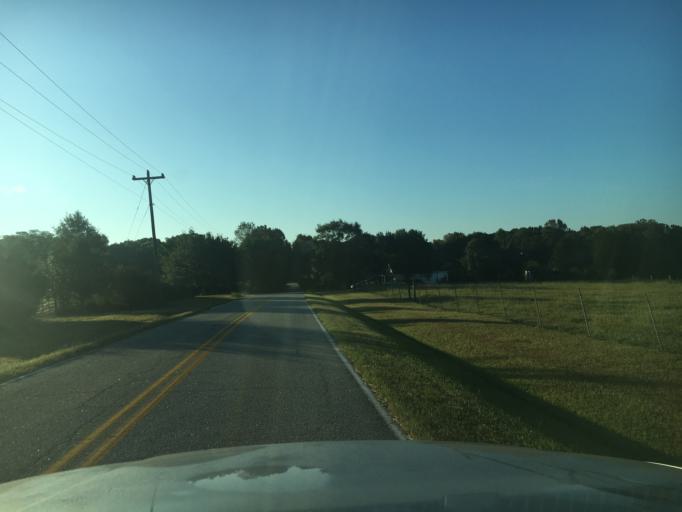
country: US
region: South Carolina
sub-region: Spartanburg County
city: Woodruff
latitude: 34.7908
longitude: -82.0073
